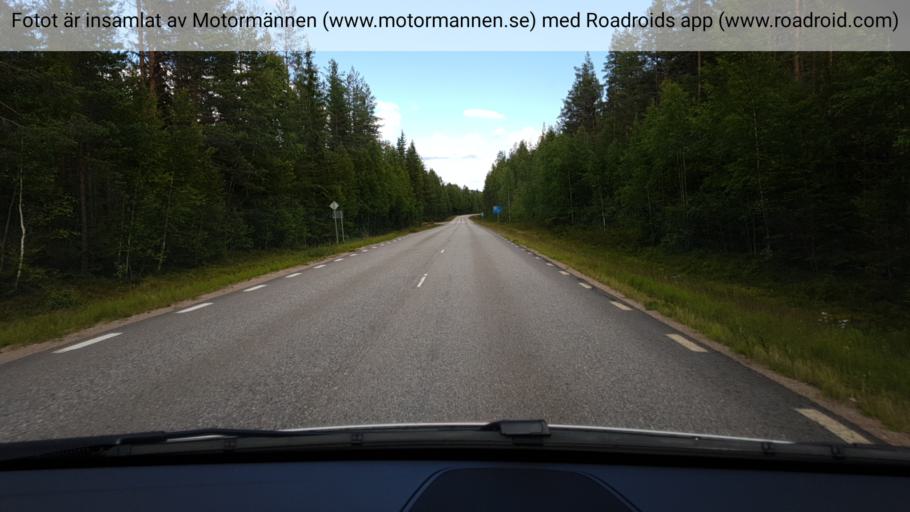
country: SE
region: Jaemtland
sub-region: Harjedalens Kommun
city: Sveg
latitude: 61.9797
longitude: 15.0979
